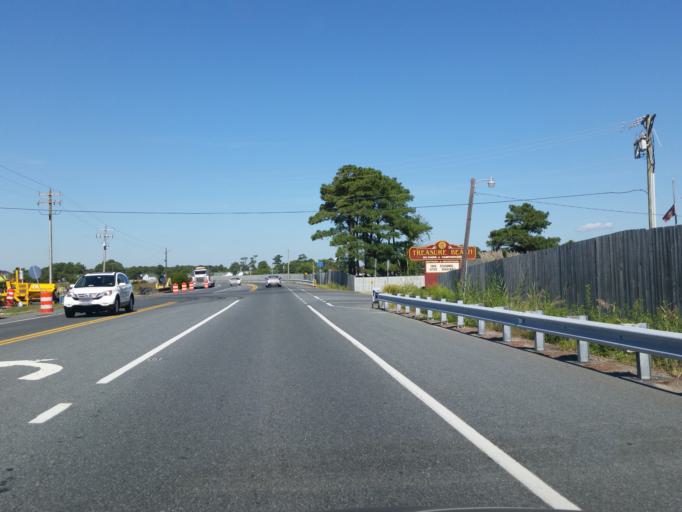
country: US
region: Delaware
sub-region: Sussex County
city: Bethany Beach
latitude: 38.4623
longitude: -75.0794
